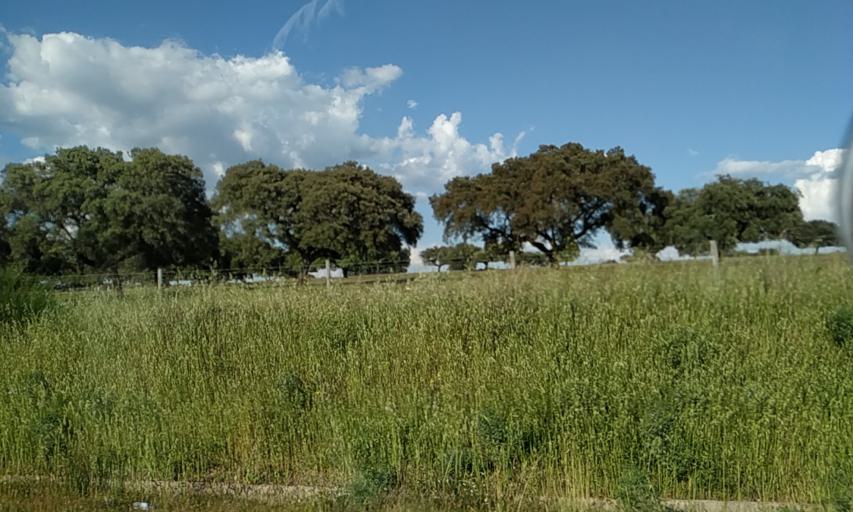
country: PT
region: Portalegre
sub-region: Portalegre
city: Urra
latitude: 39.1447
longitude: -7.4520
